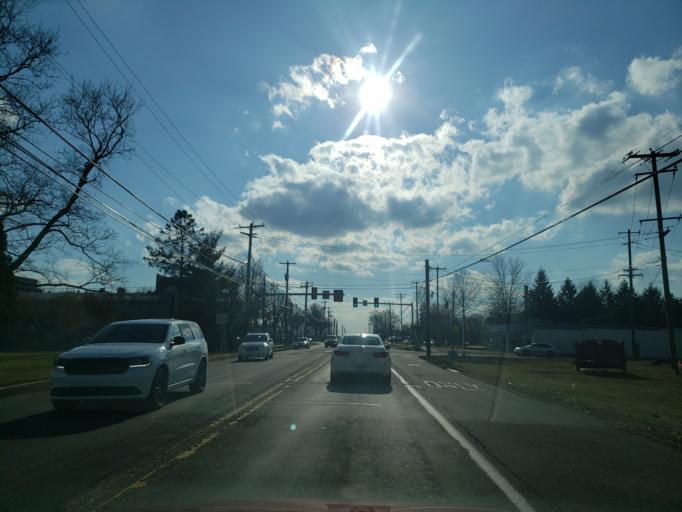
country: US
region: Pennsylvania
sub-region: Montgomery County
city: Blue Bell
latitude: 40.1558
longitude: -75.3016
